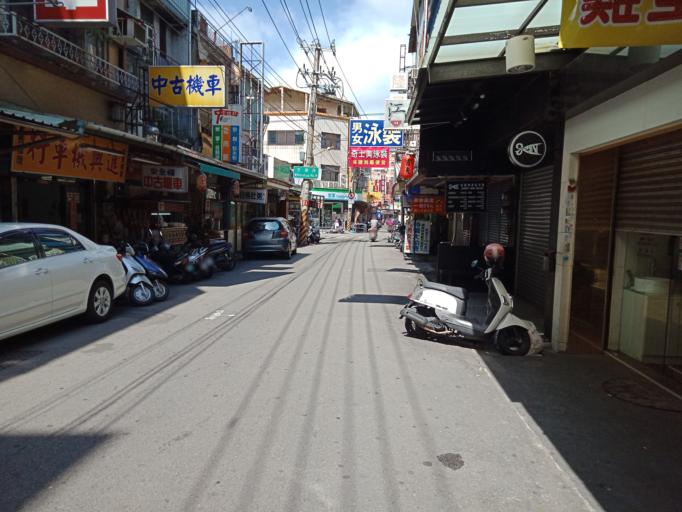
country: TW
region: Taiwan
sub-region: Taichung City
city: Taichung
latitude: 24.1751
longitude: 120.6453
